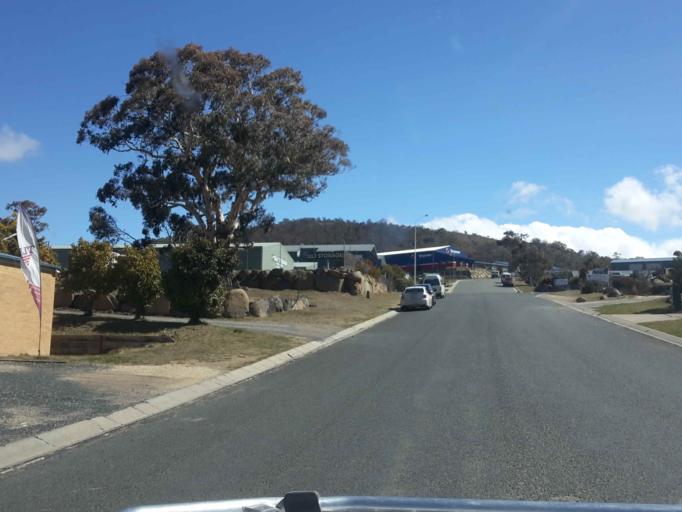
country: AU
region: New South Wales
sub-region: Snowy River
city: Jindabyne
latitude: -36.4376
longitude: 148.6021
